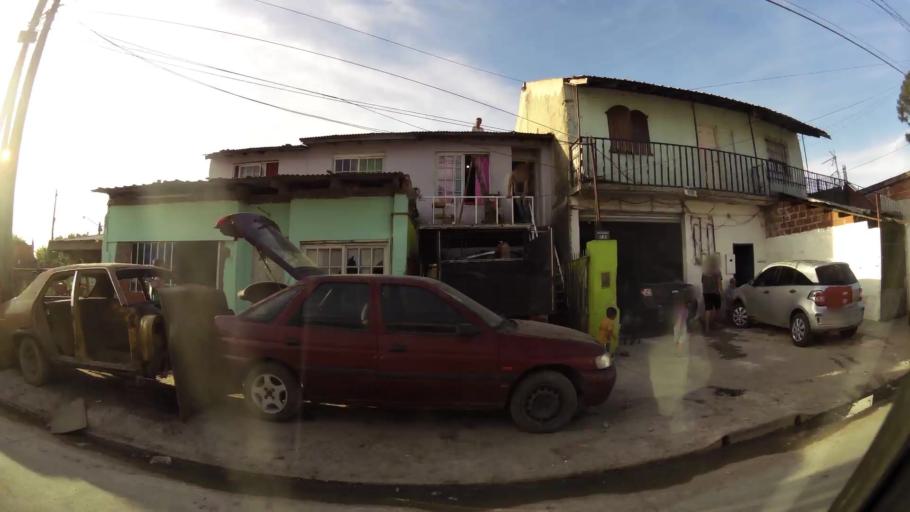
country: AR
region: Buenos Aires
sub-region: Partido de Almirante Brown
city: Adrogue
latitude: -34.7928
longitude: -58.3255
